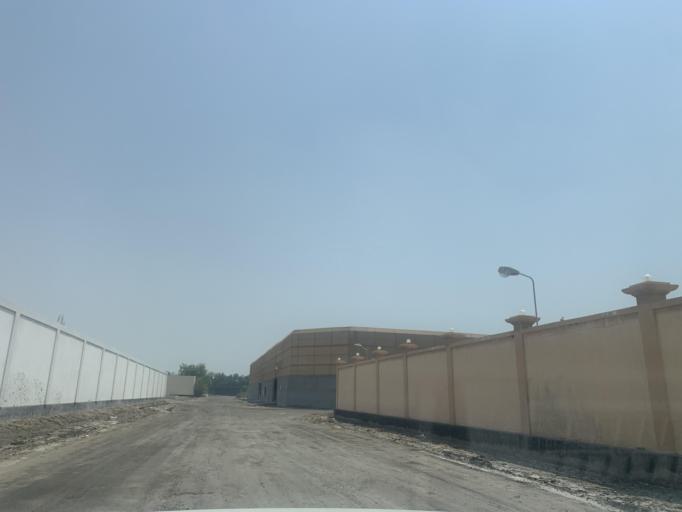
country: BH
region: Central Governorate
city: Madinat Hamad
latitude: 26.1256
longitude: 50.4686
